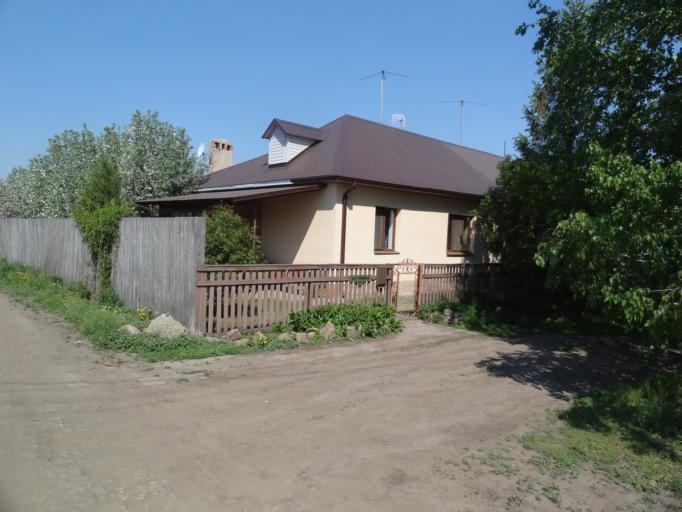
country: RU
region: Saratov
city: Privolzhskiy
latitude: 51.4138
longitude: 46.0991
